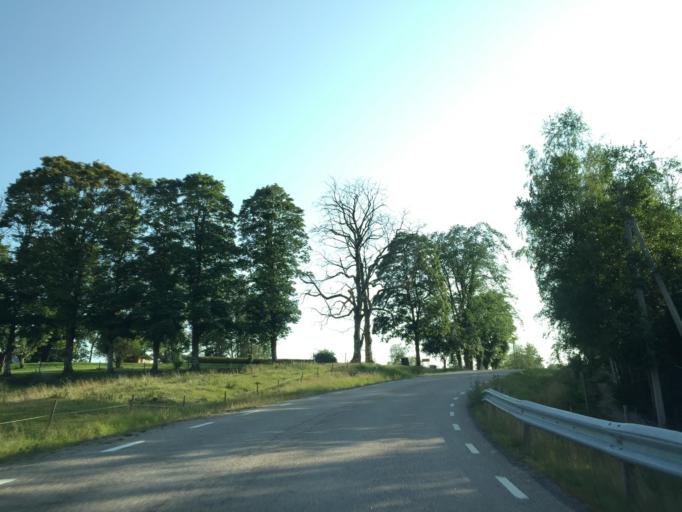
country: SE
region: Vaestra Goetaland
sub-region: Lilla Edets Kommun
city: Lilla Edet
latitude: 58.1666
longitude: 12.0754
